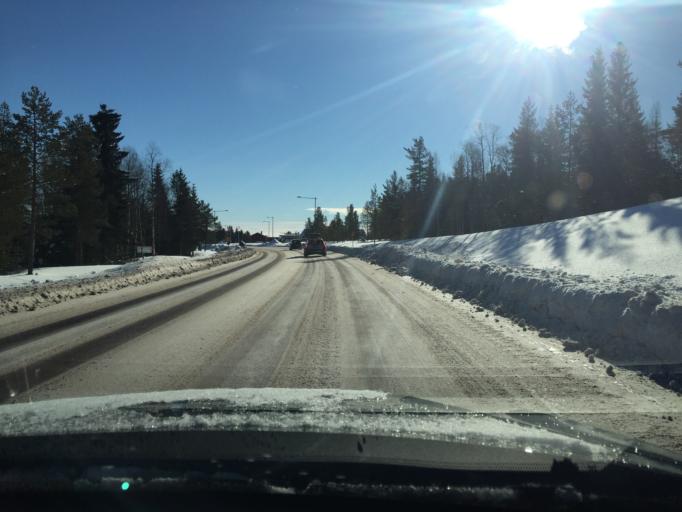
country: SE
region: Dalarna
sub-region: Malung-Saelens kommun
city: Malung
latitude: 61.1662
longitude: 13.1955
